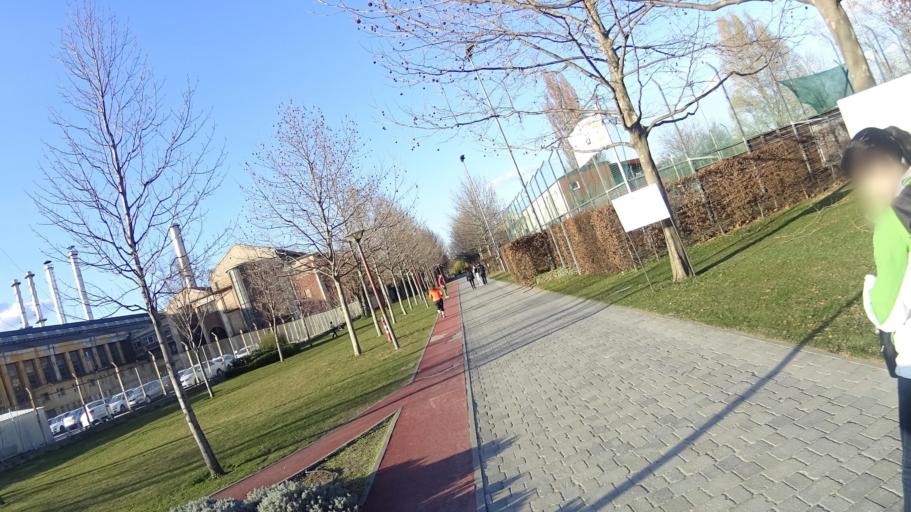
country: HU
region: Budapest
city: Budapest IX. keruelet
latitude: 47.4606
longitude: 19.0574
